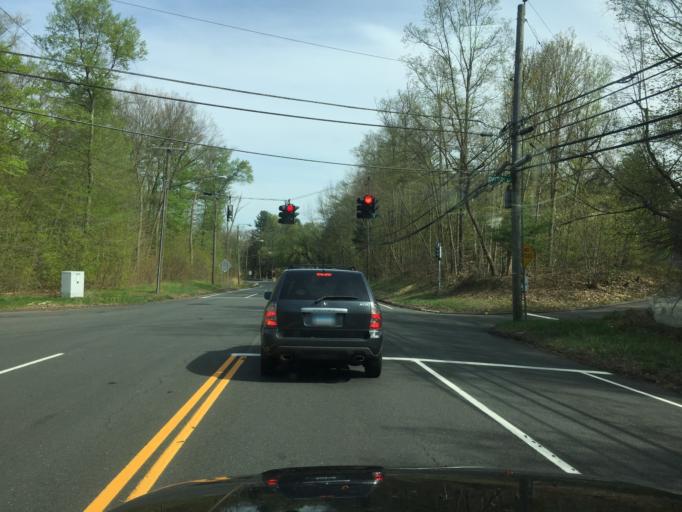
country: US
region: Connecticut
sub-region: Hartford County
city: West Hartford
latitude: 41.7898
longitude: -72.7753
